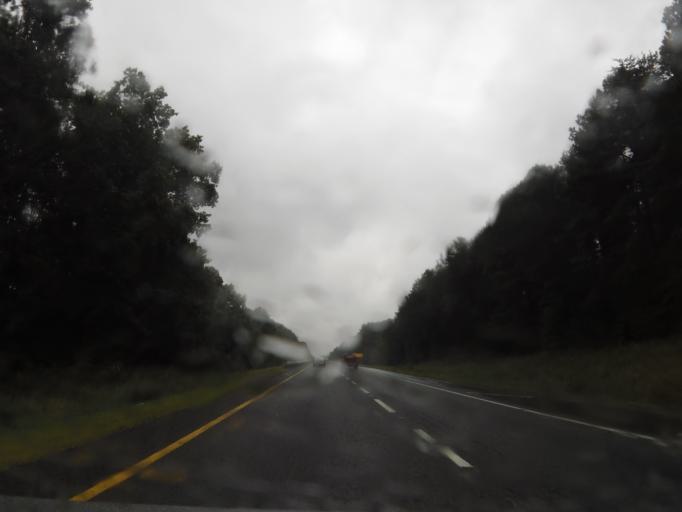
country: US
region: Tennessee
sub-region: Bradley County
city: Hopewell
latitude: 35.2701
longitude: -84.8268
